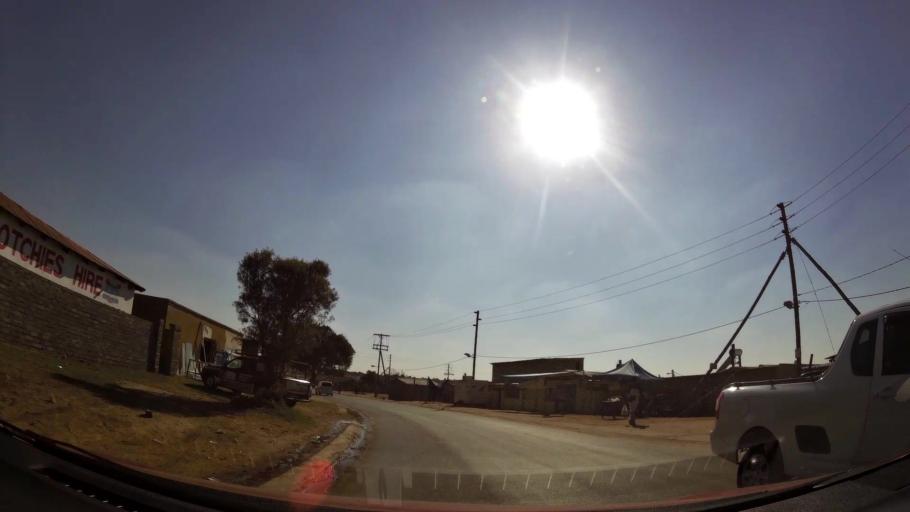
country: ZA
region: Gauteng
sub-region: West Rand District Municipality
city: Muldersdriseloop
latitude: -26.0164
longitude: 27.9276
